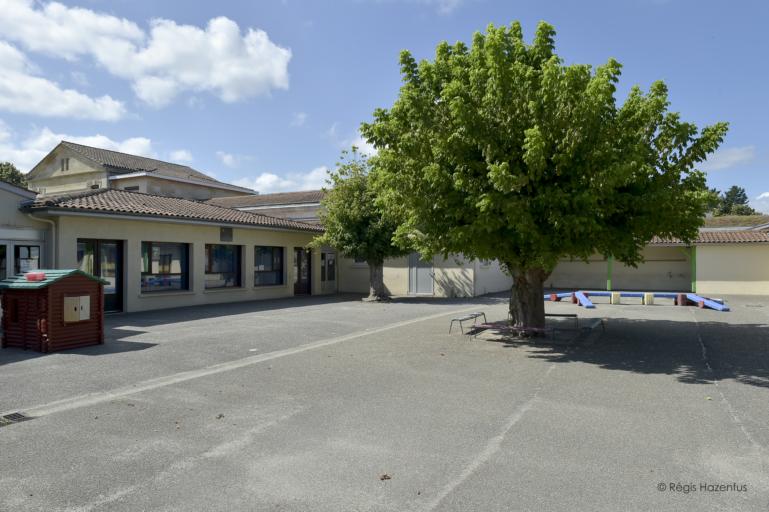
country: FR
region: Aquitaine
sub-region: Departement de la Gironde
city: Villenave-d'Ornon
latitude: 44.7700
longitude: -0.5447
